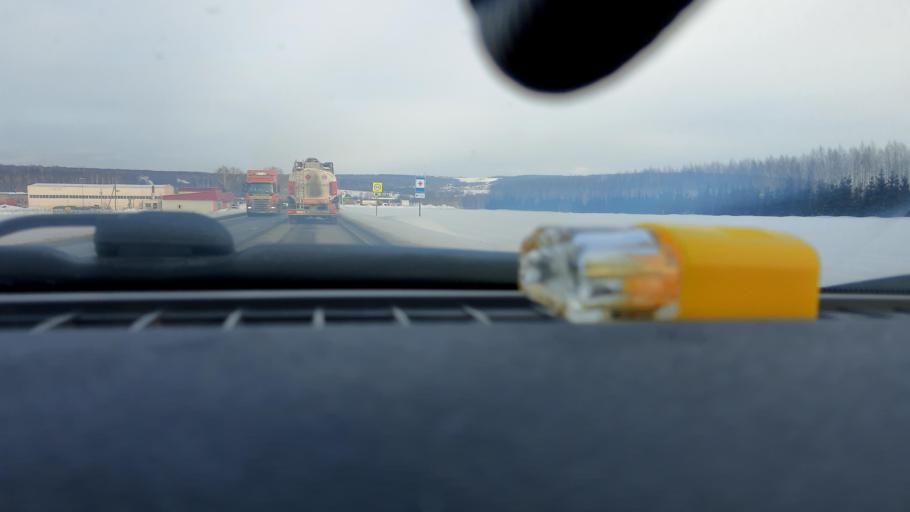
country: RU
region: Bashkortostan
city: Iglino
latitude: 54.7600
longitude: 56.3826
